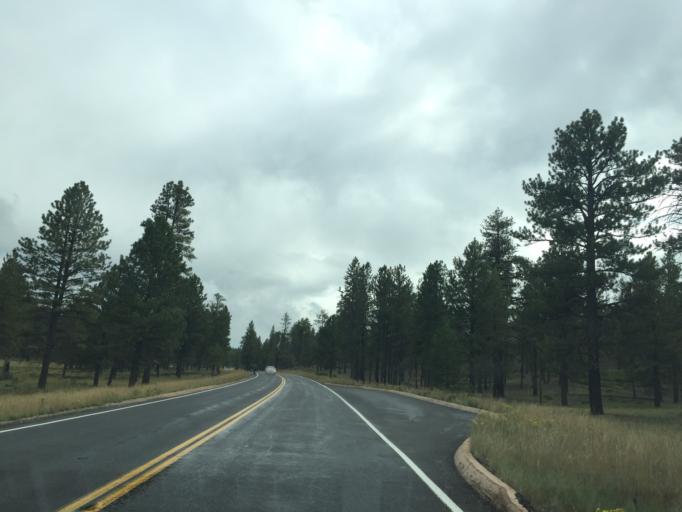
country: US
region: Utah
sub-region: Garfield County
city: Panguitch
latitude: 37.6323
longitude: -112.1737
